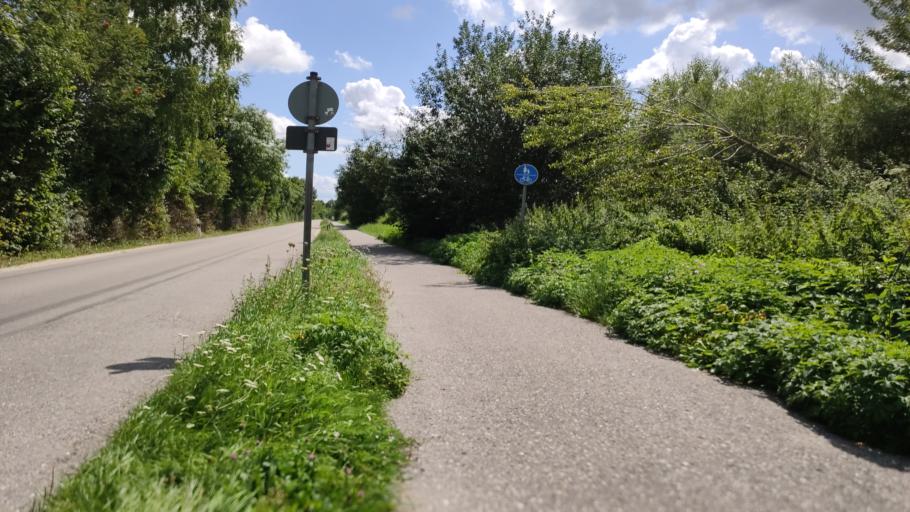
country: DE
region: Bavaria
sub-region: Swabia
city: Konigsbrunn
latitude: 48.2480
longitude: 10.8926
